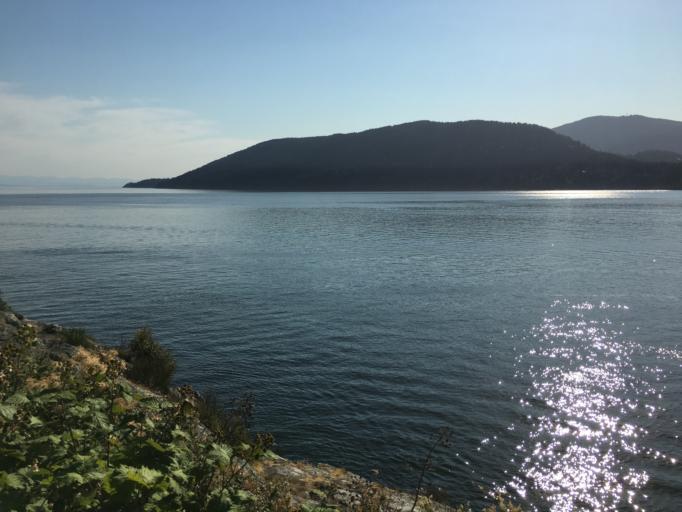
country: CA
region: British Columbia
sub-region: Greater Vancouver Regional District
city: Bowen Island
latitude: 49.3730
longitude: -123.2931
